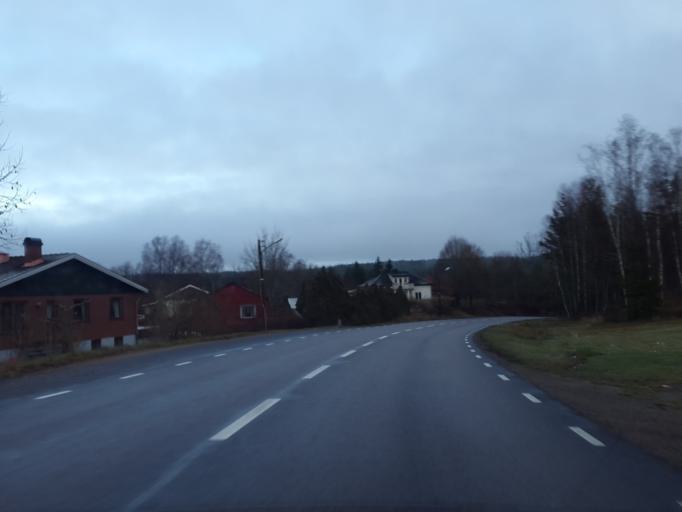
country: SE
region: Vaestra Goetaland
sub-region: Boras Kommun
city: Sandared
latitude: 57.8086
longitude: 12.7521
